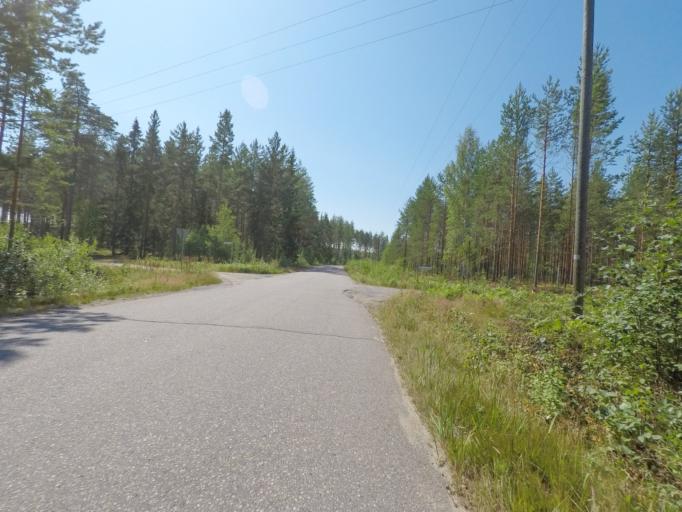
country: FI
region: Southern Savonia
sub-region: Mikkeli
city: Puumala
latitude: 61.4255
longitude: 28.1574
